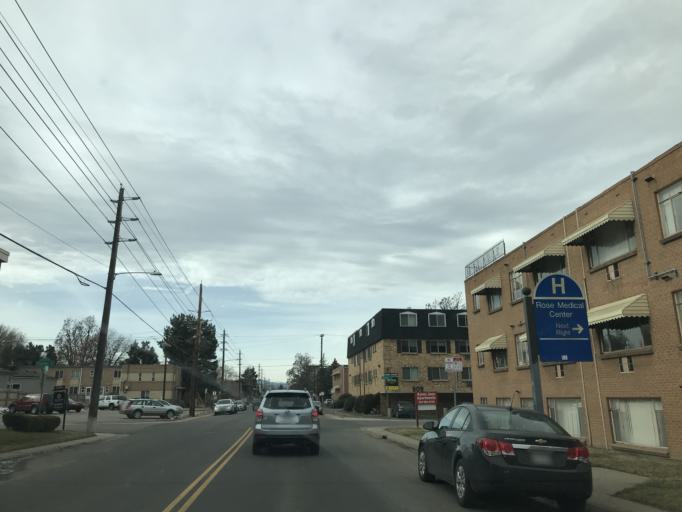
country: US
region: Colorado
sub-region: Arapahoe County
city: Glendale
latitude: 39.7293
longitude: -104.9323
